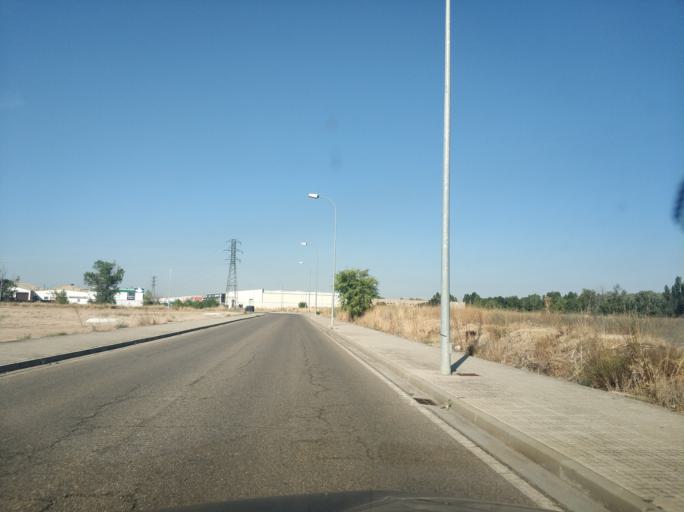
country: ES
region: Castille and Leon
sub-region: Provincia de Burgos
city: Aranda de Duero
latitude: 41.6722
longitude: -3.7010
